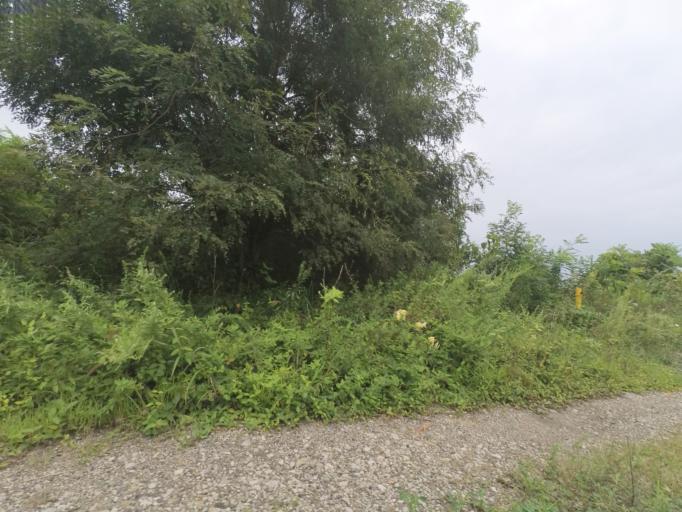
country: US
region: West Virginia
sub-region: Cabell County
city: Huntington
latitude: 38.4291
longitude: -82.4206
